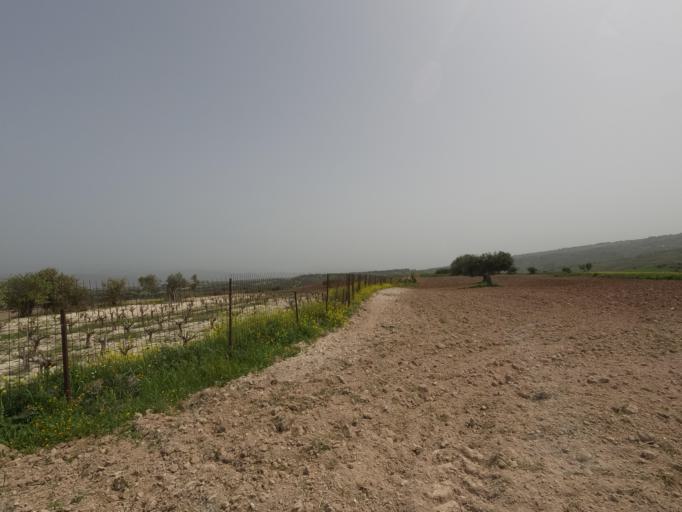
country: CY
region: Pafos
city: Polis
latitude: 34.9924
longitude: 32.3890
